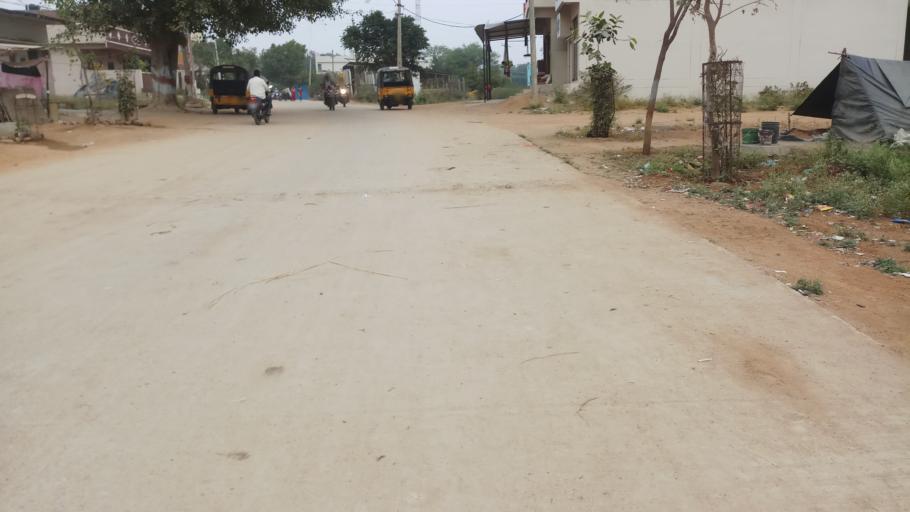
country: IN
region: Telangana
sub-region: Rangareddi
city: Quthbullapur
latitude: 17.6688
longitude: 78.4704
